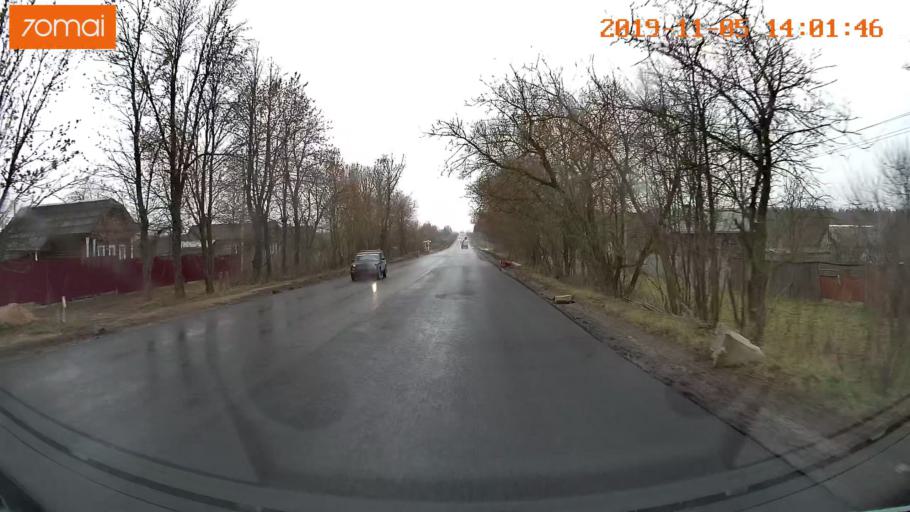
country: RU
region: Ivanovo
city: Kokhma
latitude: 57.0069
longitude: 41.2251
